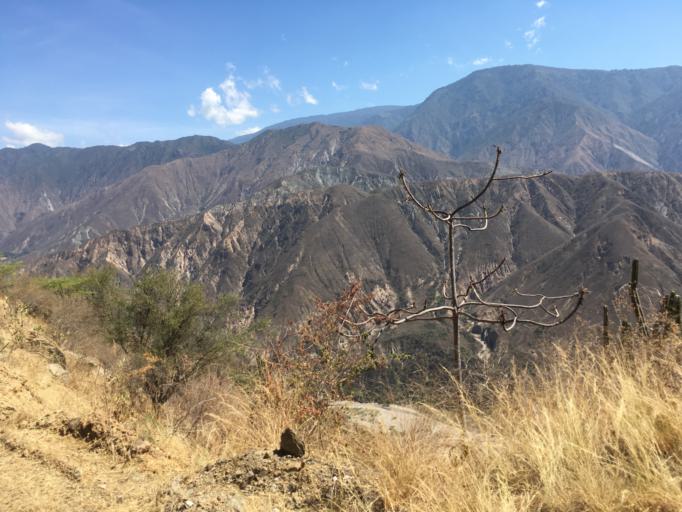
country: CO
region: Santander
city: Aratoca
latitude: 6.7803
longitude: -72.9938
